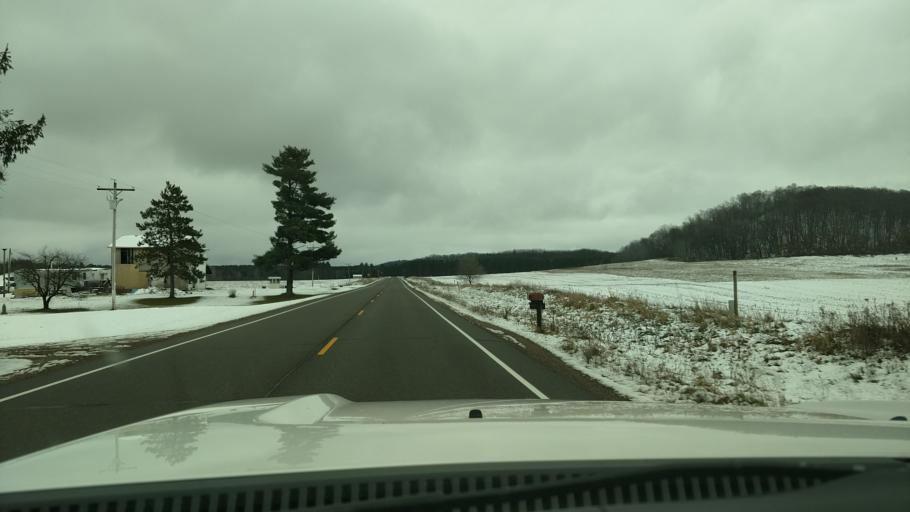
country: US
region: Wisconsin
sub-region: Dunn County
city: Colfax
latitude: 45.1390
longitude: -91.7582
